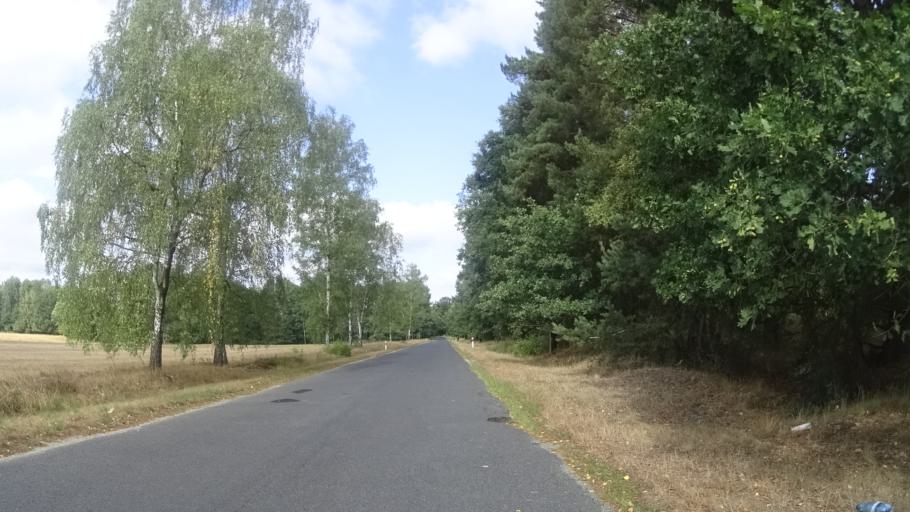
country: PL
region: Lubusz
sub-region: Powiat zarski
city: Przewoz
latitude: 51.4907
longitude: 14.8776
